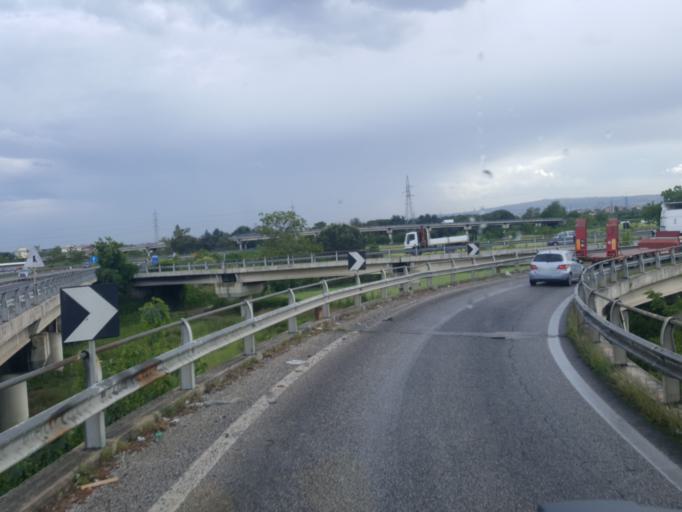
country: IT
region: Campania
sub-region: Provincia di Napoli
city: Pascarola
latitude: 40.9722
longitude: 14.2930
